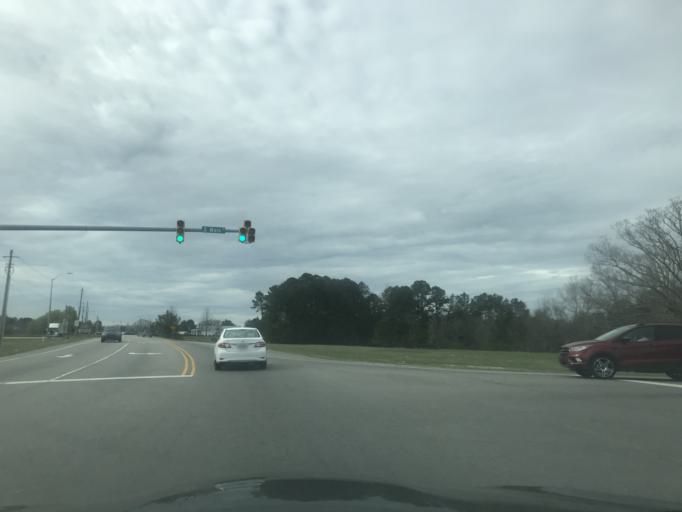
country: US
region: North Carolina
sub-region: Franklin County
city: Louisburg
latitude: 36.0838
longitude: -78.3150
